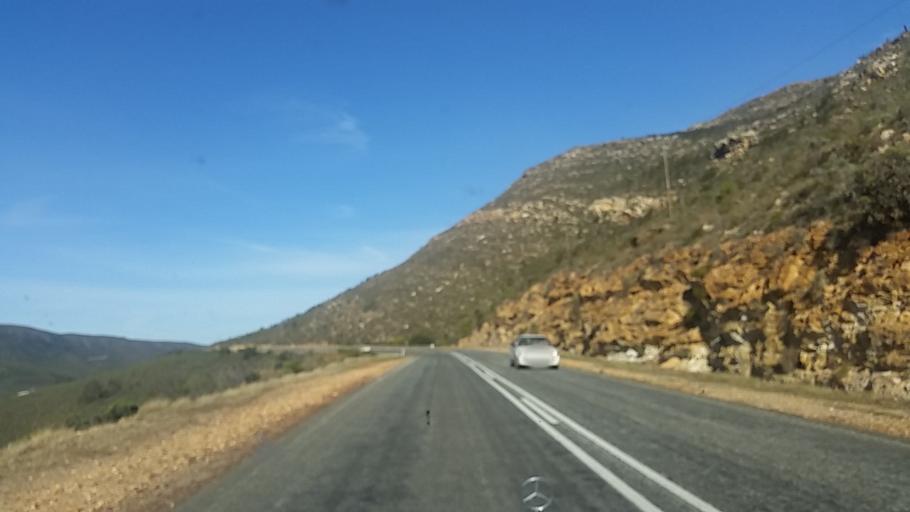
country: ZA
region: Western Cape
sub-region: Eden District Municipality
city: Knysna
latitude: -33.7482
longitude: 22.9769
